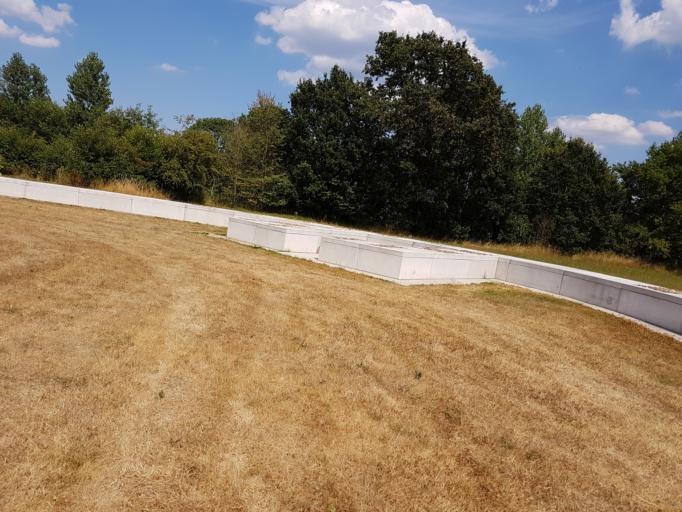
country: NL
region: Utrecht
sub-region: Gemeente Utrecht
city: Lunetten
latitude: 52.0575
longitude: 5.1632
